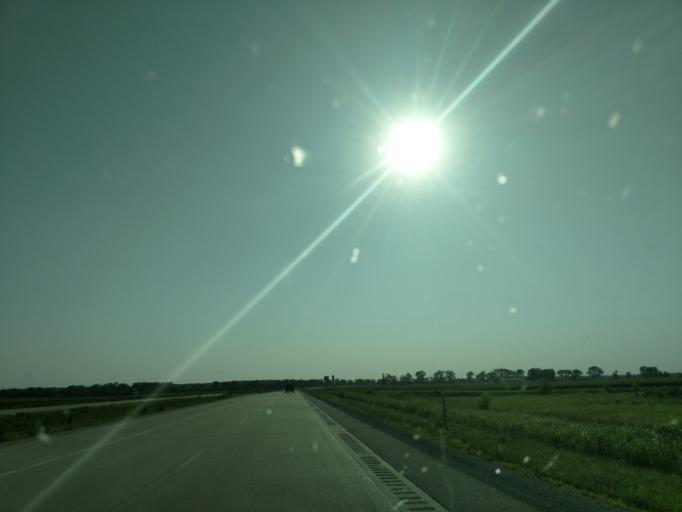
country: US
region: Nebraska
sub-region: Cass County
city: Plattsmouth
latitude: 41.0442
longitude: -95.8403
